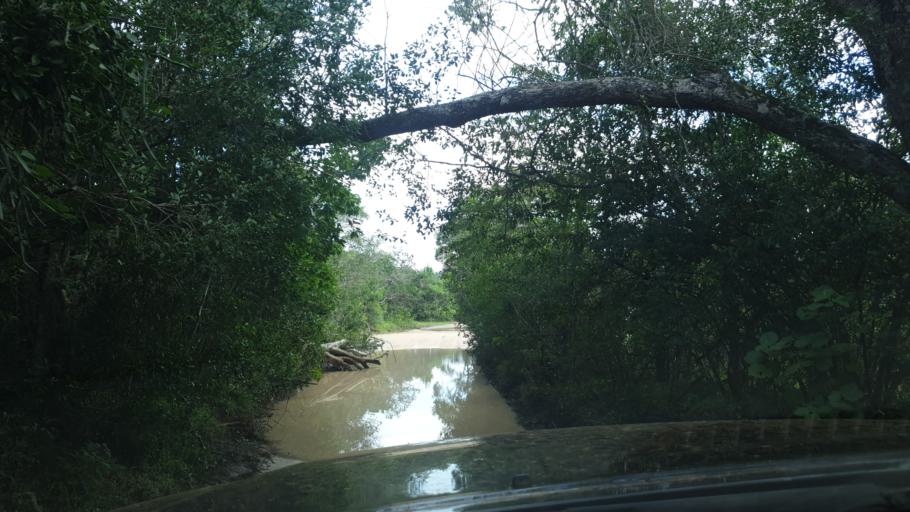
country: LK
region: North Central
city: Anuradhapura
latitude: 8.4271
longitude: 80.0193
